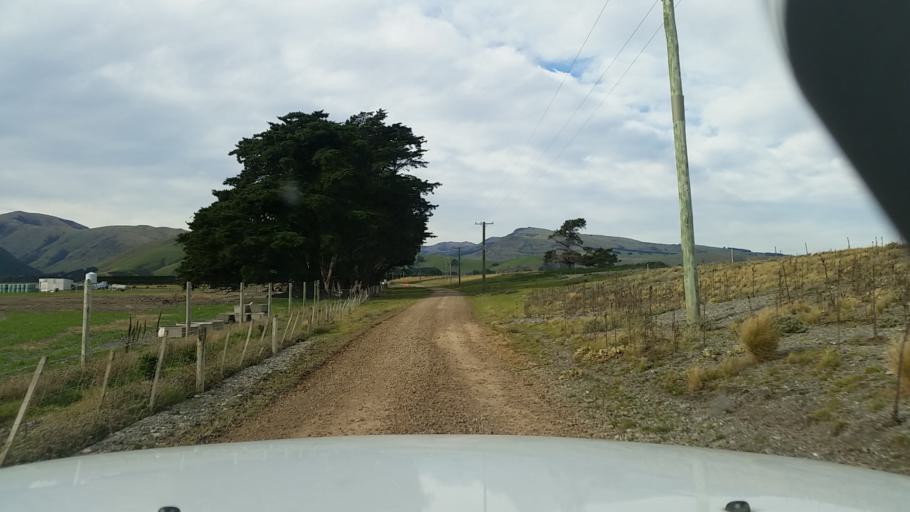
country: NZ
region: Canterbury
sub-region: Selwyn District
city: Lincoln
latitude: -43.8117
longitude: 172.6612
